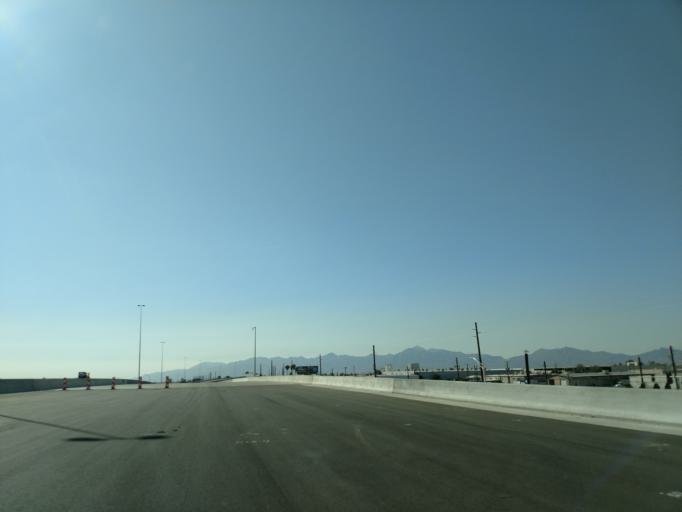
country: US
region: Arizona
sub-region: Maricopa County
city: Tolleson
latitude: 33.4523
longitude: -112.1859
